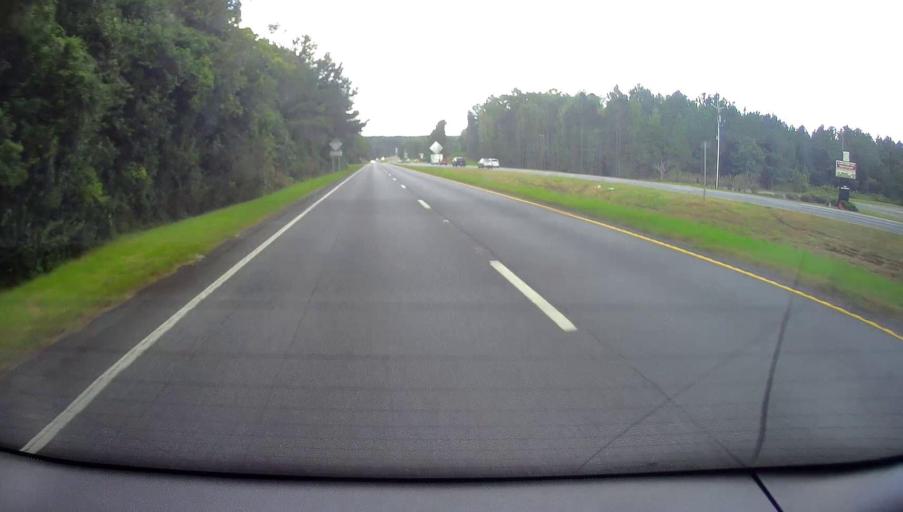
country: US
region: Georgia
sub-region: Bibb County
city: Macon
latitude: 32.9100
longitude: -83.5909
